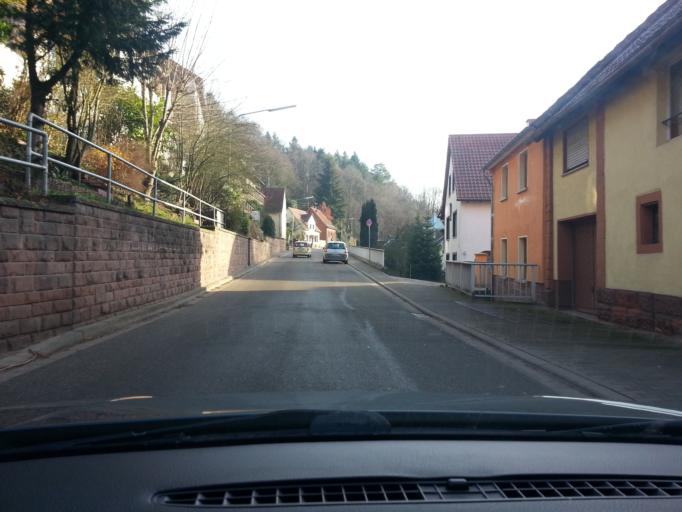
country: DE
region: Rheinland-Pfalz
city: Gossersweiler-Stein
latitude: 49.1568
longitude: 7.9398
